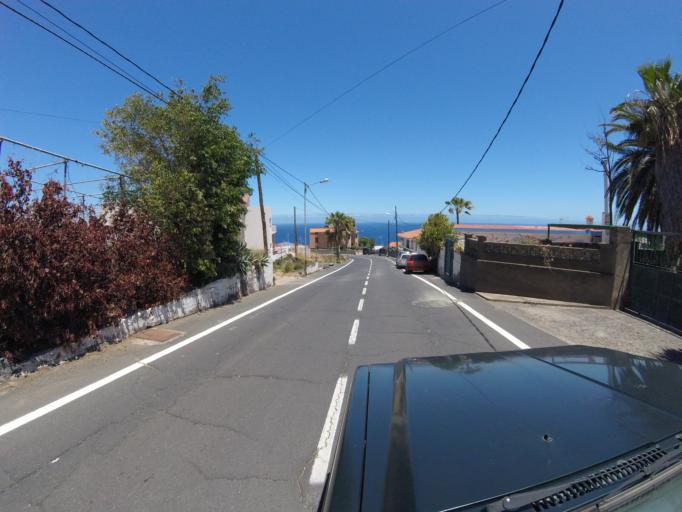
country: ES
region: Canary Islands
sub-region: Provincia de Santa Cruz de Tenerife
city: Candelaria
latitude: 28.3633
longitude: -16.3757
